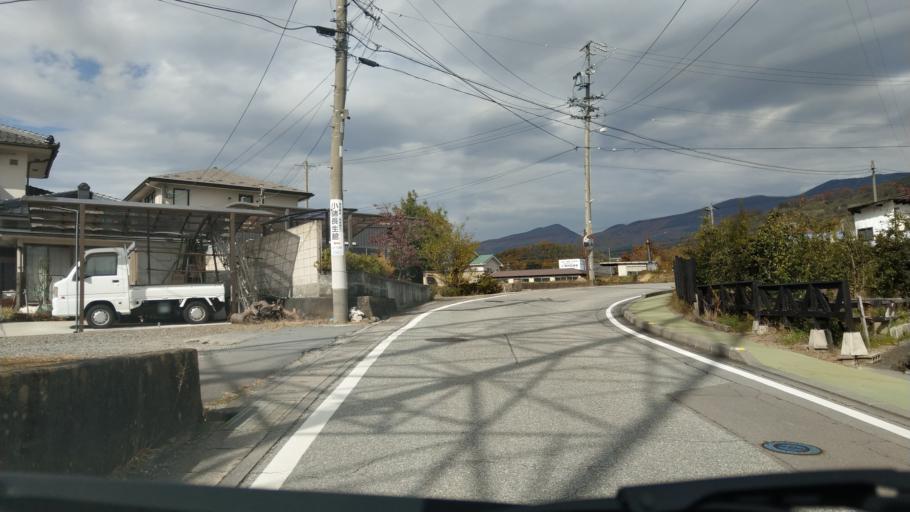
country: JP
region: Nagano
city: Komoro
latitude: 36.3348
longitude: 138.4160
